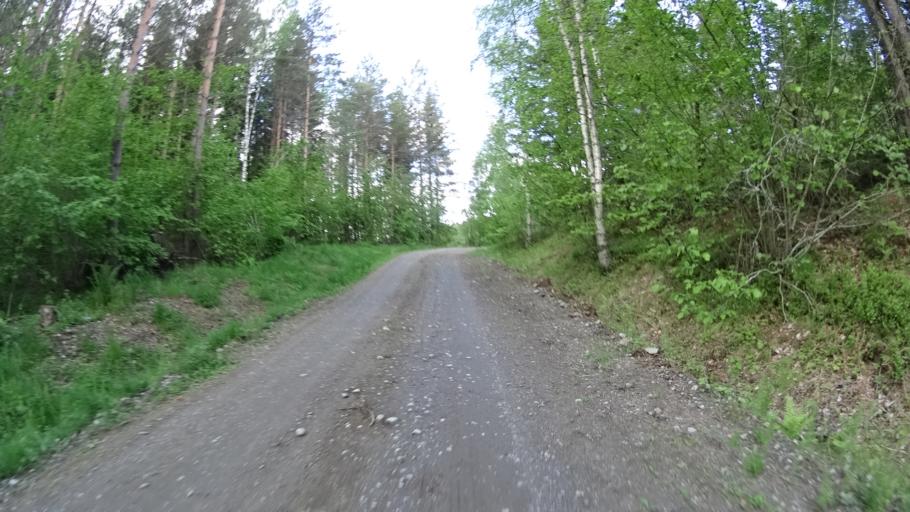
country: FI
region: Uusimaa
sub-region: Raaseporin
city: Karis
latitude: 60.1527
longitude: 23.6228
